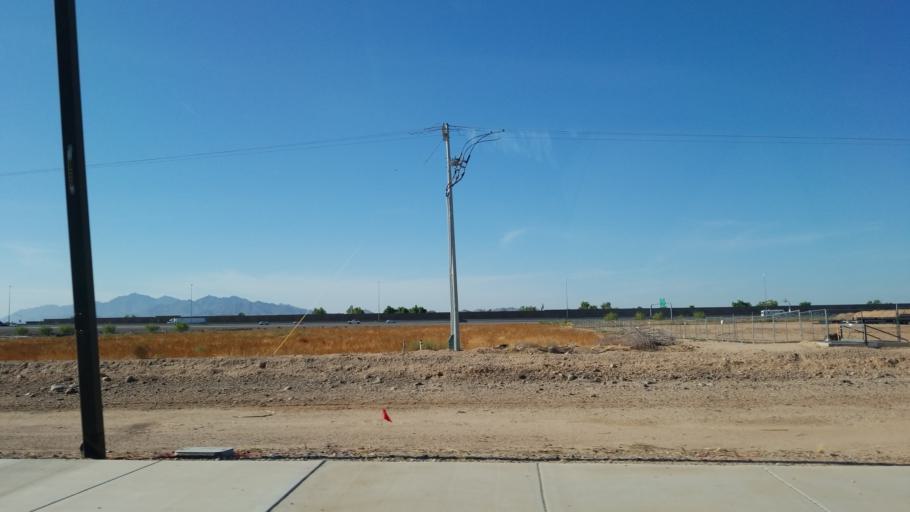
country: US
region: Arizona
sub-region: Maricopa County
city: Litchfield Park
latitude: 33.4647
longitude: -112.3980
